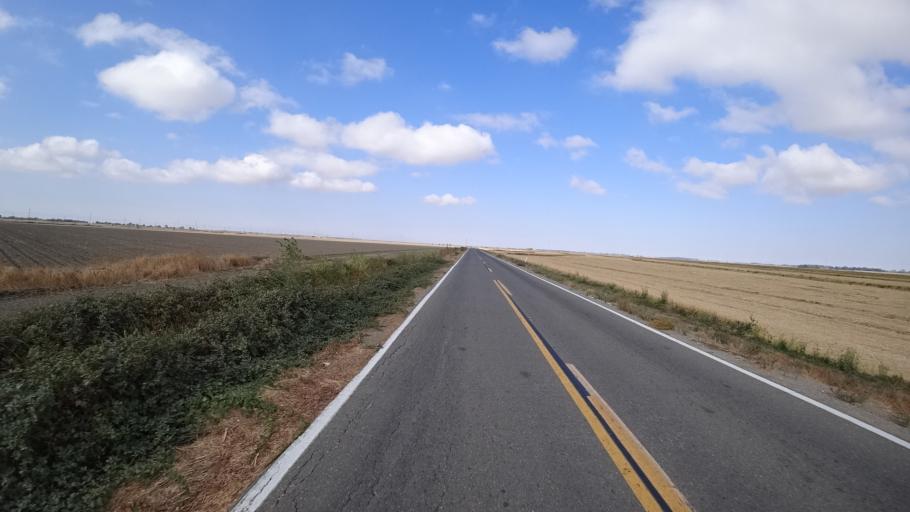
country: US
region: California
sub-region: Yolo County
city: Woodland
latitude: 38.8067
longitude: -121.7279
